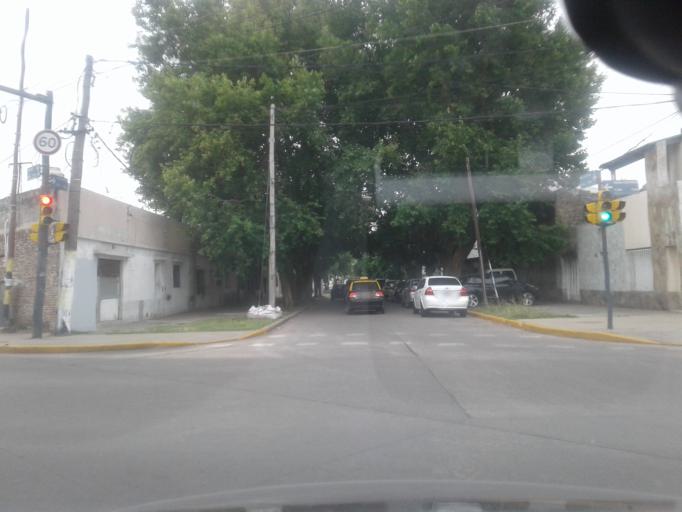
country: AR
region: Santa Fe
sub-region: Departamento de Rosario
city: Rosario
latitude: -32.9251
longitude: -60.6820
